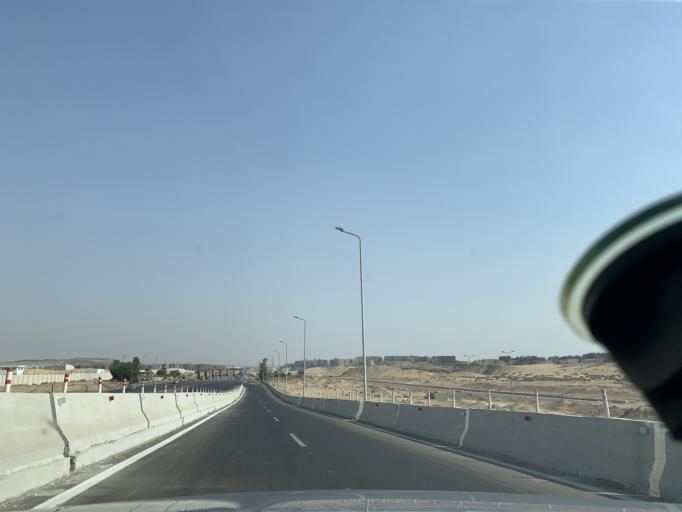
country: EG
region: Muhafazat al Qalyubiyah
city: Al Khankah
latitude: 30.2006
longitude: 31.4200
